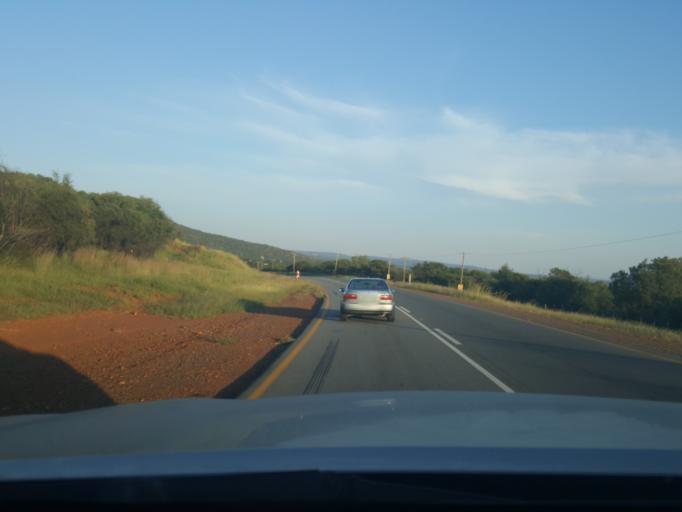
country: ZA
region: North-West
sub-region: Ngaka Modiri Molema District Municipality
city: Zeerust
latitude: -25.5210
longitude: 26.0675
